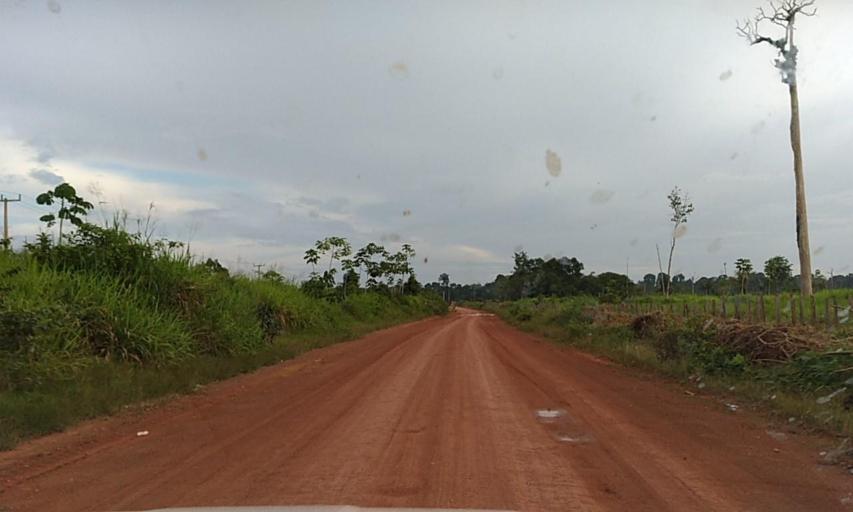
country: BR
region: Para
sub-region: Senador Jose Porfirio
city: Senador Jose Porfirio
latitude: -2.6927
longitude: -51.8246
